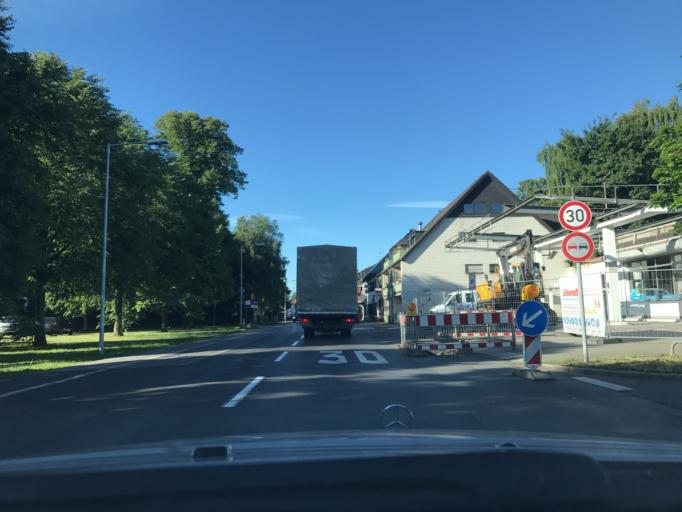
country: DE
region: North Rhine-Westphalia
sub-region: Regierungsbezirk Dusseldorf
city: Krefeld
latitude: 51.3832
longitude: 6.5996
